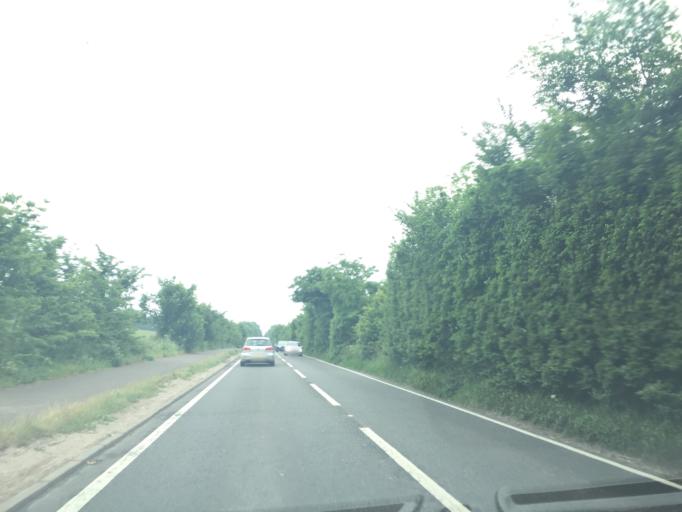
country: GB
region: England
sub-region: Dorset
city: Dorchester
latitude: 50.6978
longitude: -2.4489
